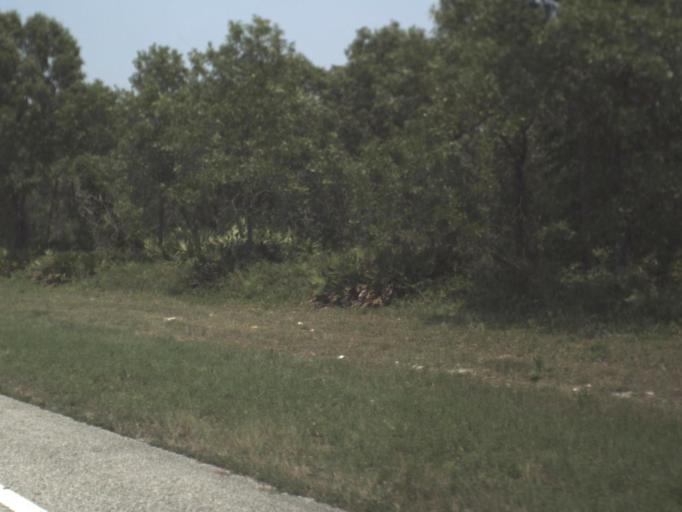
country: US
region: Florida
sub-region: Baker County
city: Macclenny
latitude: 30.1325
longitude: -82.0399
